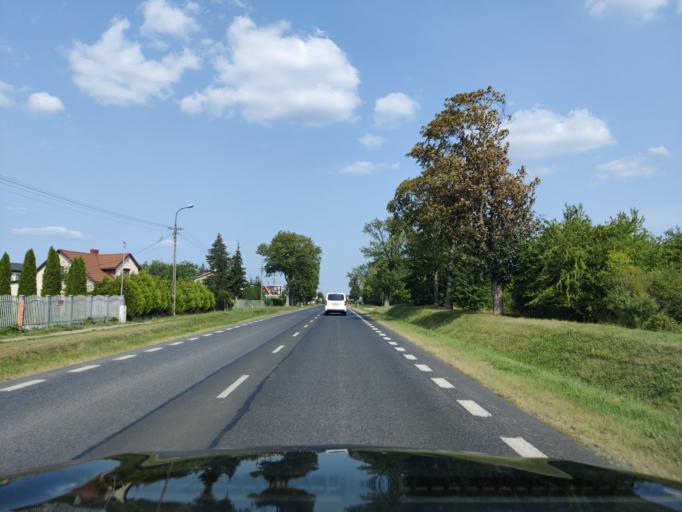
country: PL
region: Masovian Voivodeship
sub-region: Powiat makowski
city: Rozan
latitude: 52.8854
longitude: 21.3855
